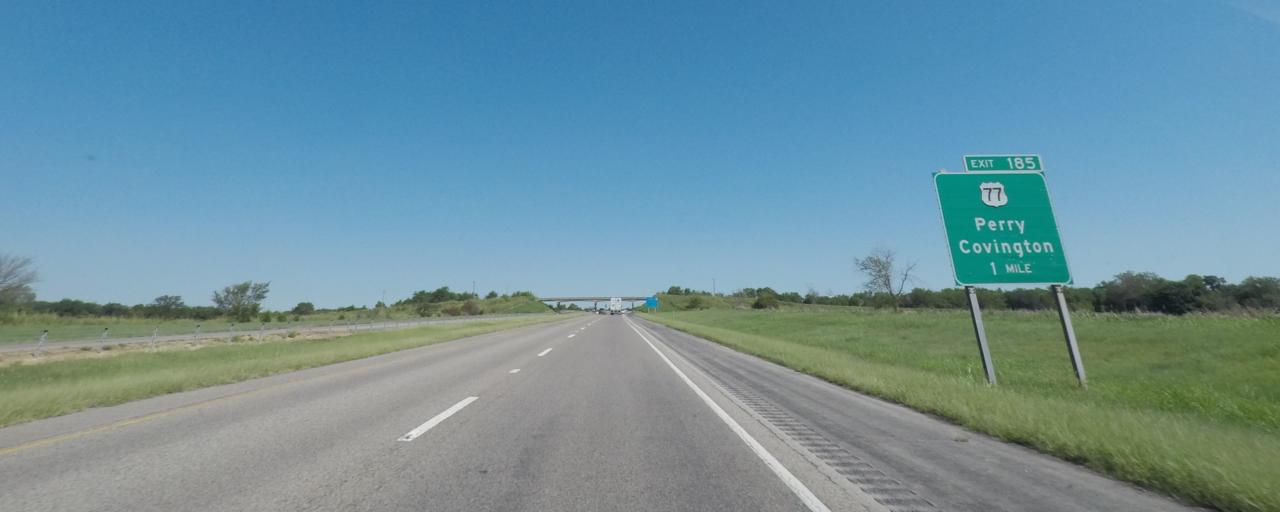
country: US
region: Oklahoma
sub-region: Noble County
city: Perry
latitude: 36.2577
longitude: -97.3258
